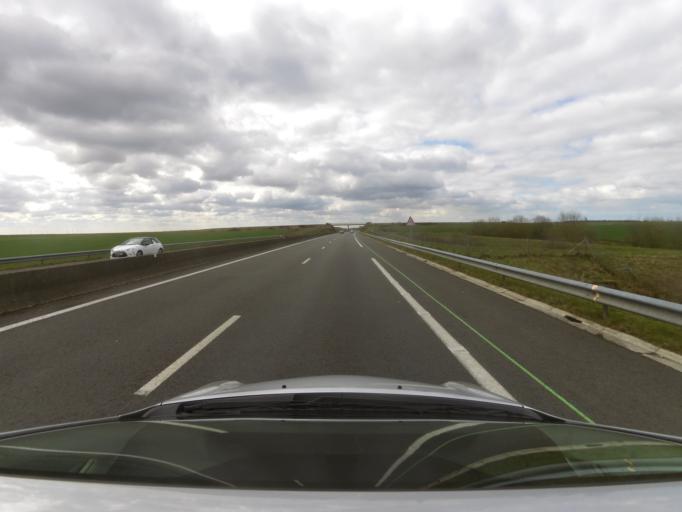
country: FR
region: Nord-Pas-de-Calais
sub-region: Departement du Pas-de-Calais
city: Verton
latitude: 50.3697
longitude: 1.6945
